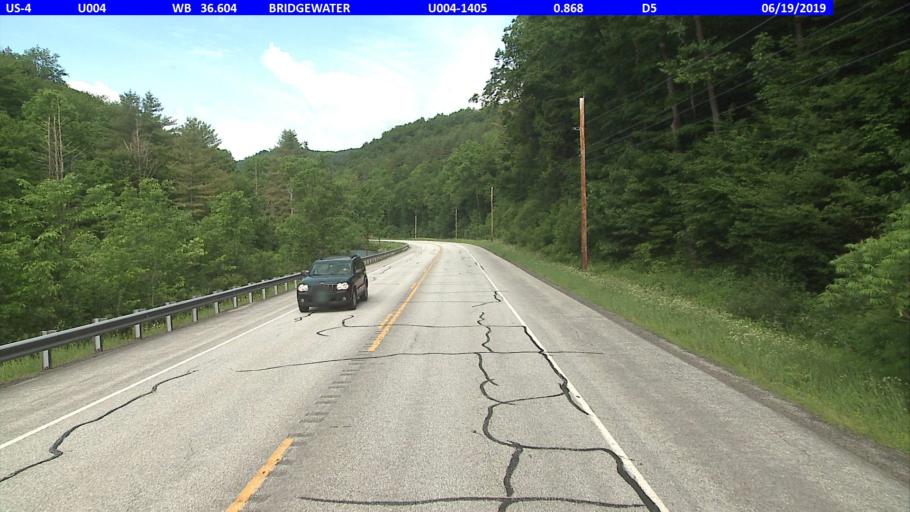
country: US
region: Vermont
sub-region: Windsor County
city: Woodstock
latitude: 43.6041
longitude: -72.7343
